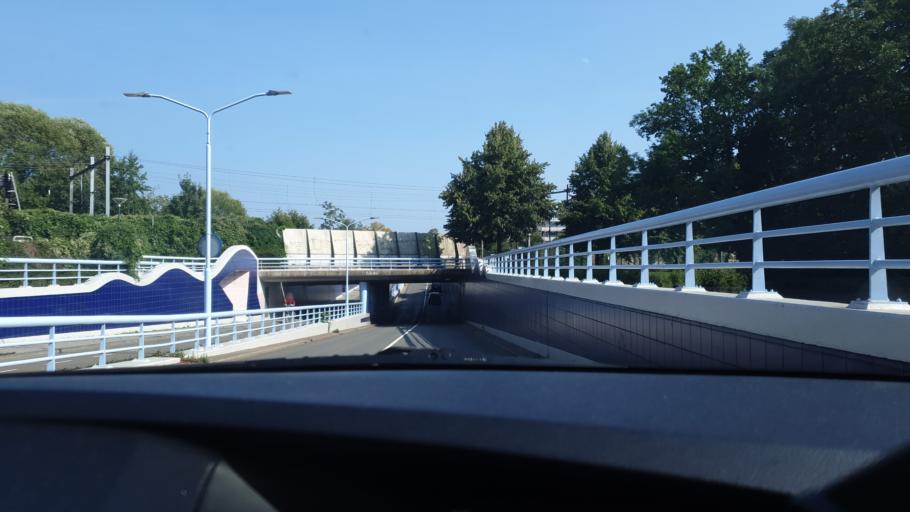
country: NL
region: South Holland
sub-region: Gemeente Dordrecht
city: Dordrecht
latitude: 51.8031
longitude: 4.6778
